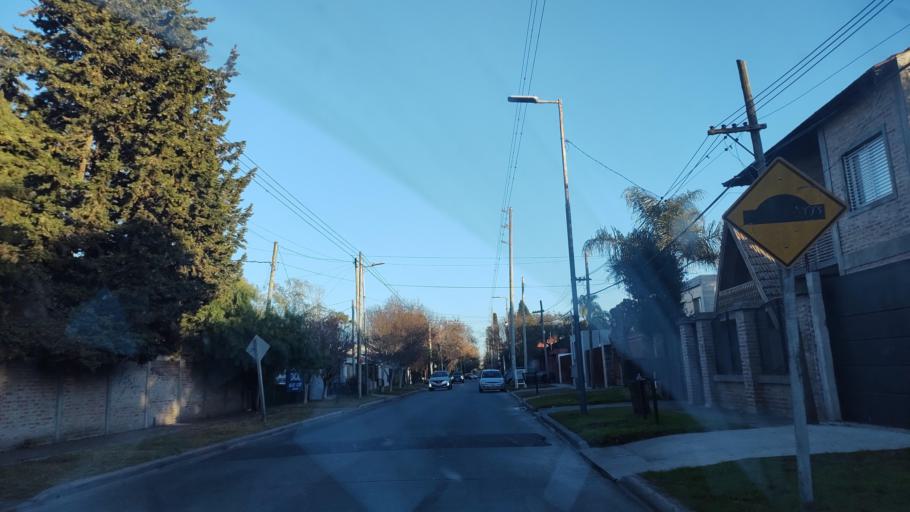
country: AR
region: Buenos Aires
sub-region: Partido de La Plata
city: La Plata
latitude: -34.8908
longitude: -58.0269
